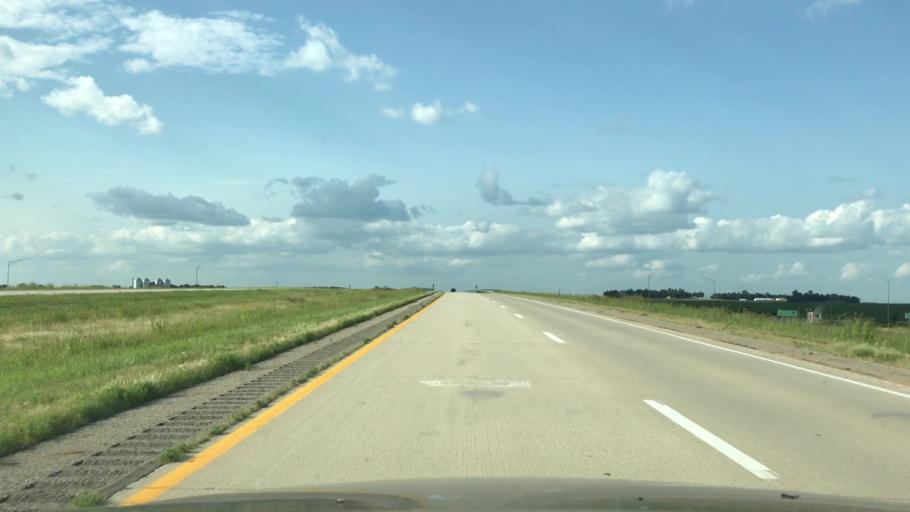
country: US
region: Iowa
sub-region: Osceola County
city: Sibley
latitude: 43.4300
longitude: -95.7138
